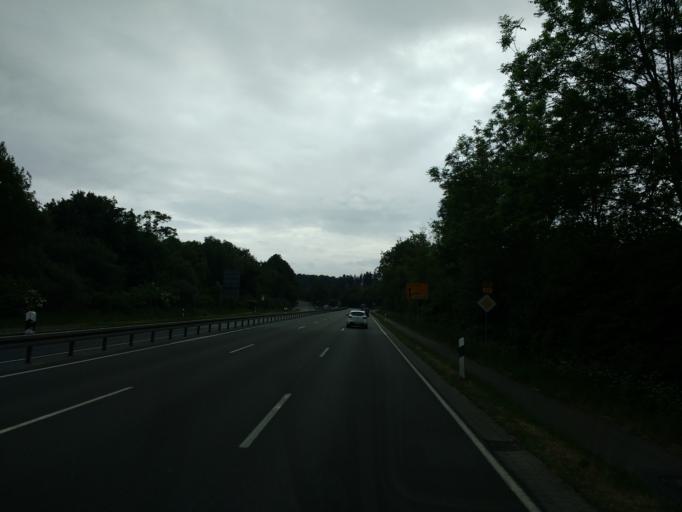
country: DE
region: Lower Saxony
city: Osnabrueck
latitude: 52.2418
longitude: 8.0607
